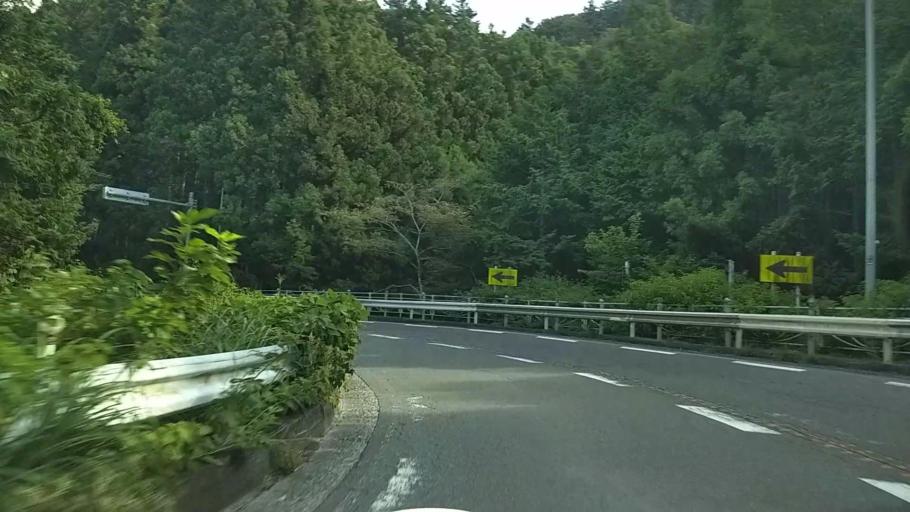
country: JP
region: Shizuoka
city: Fujinomiya
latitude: 35.3114
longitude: 138.4421
